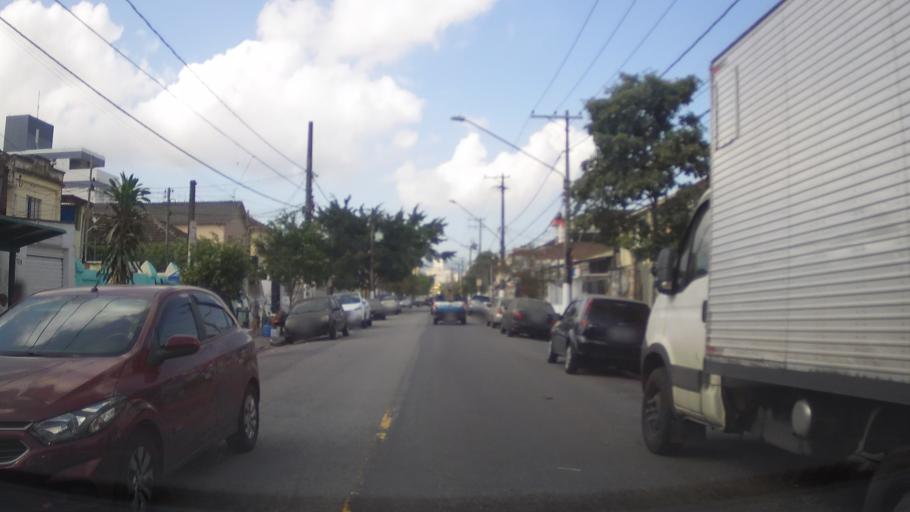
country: BR
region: Sao Paulo
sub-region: Santos
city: Santos
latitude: -23.9612
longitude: -46.3091
